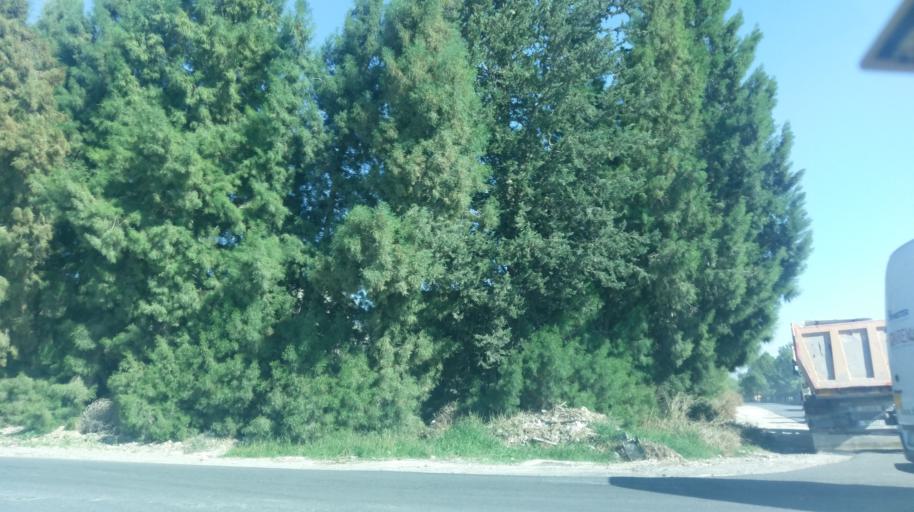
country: CY
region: Lefkosia
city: Nicosia
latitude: 35.2100
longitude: 33.4277
